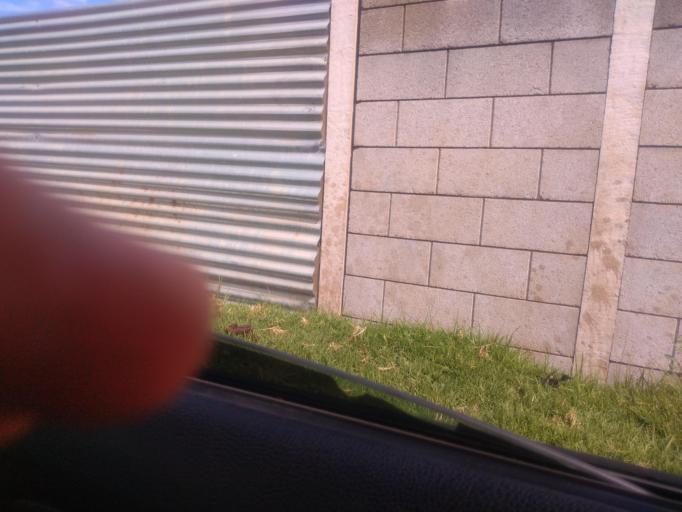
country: GT
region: Quetzaltenango
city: San Mateo
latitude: 14.8591
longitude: -91.5758
